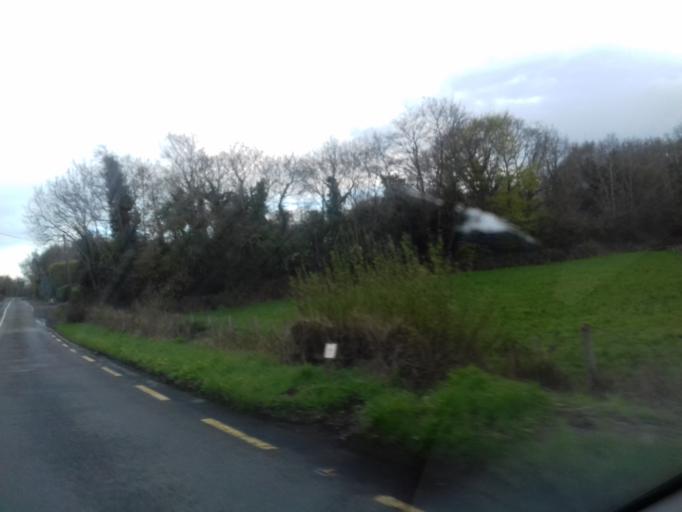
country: IE
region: Ulster
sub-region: An Cabhan
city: Ballyconnell
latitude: 54.0917
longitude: -7.5381
